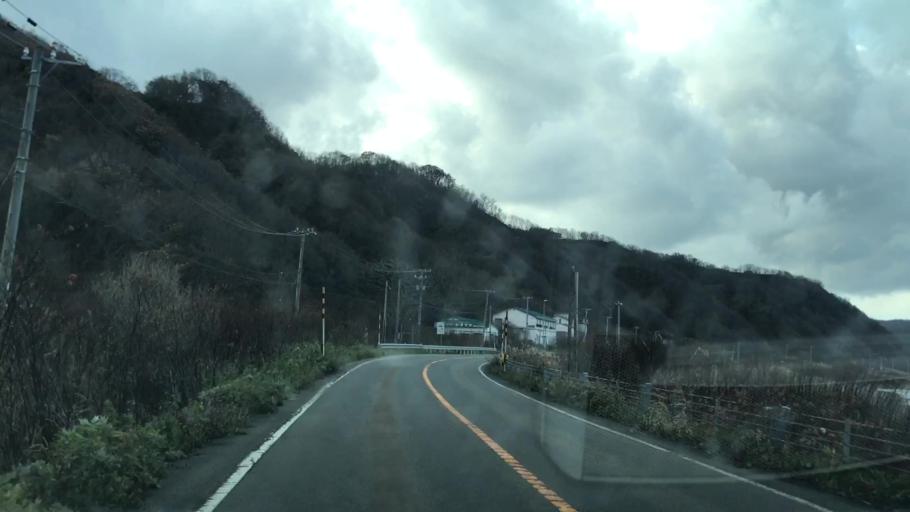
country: JP
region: Hokkaido
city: Yoichi
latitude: 43.3355
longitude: 140.4469
